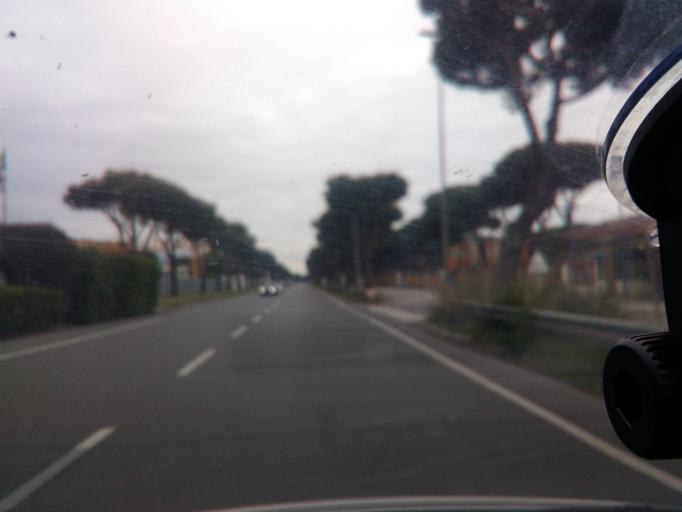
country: IT
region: Tuscany
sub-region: Provincia di Massa-Carrara
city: Massa
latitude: 44.0281
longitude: 10.1055
